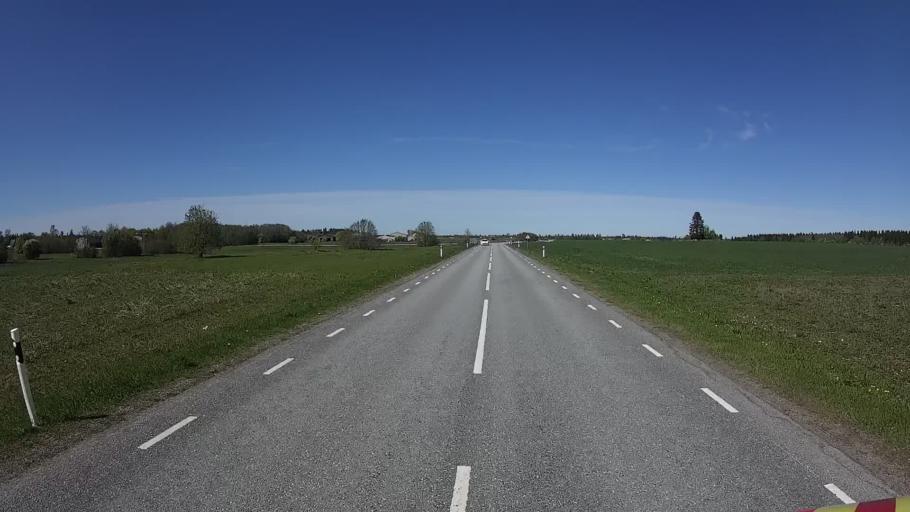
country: EE
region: Laeaene-Virumaa
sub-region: Tapa vald
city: Tapa
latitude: 59.3065
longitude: 26.0002
